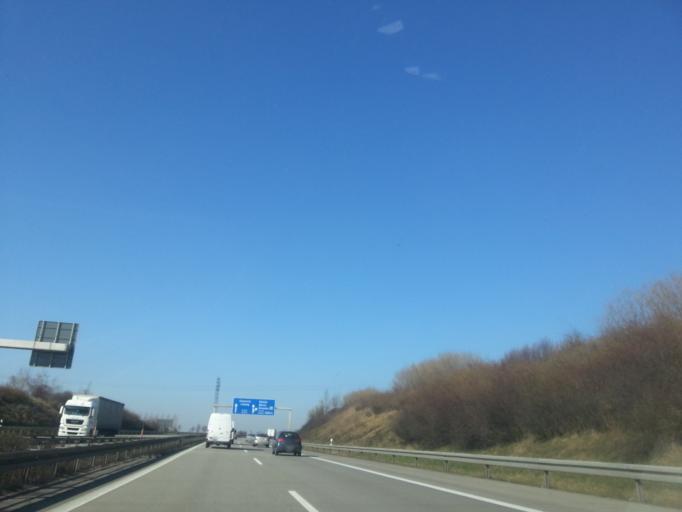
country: DE
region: Saxony
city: Freital
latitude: 51.0491
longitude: 13.6066
